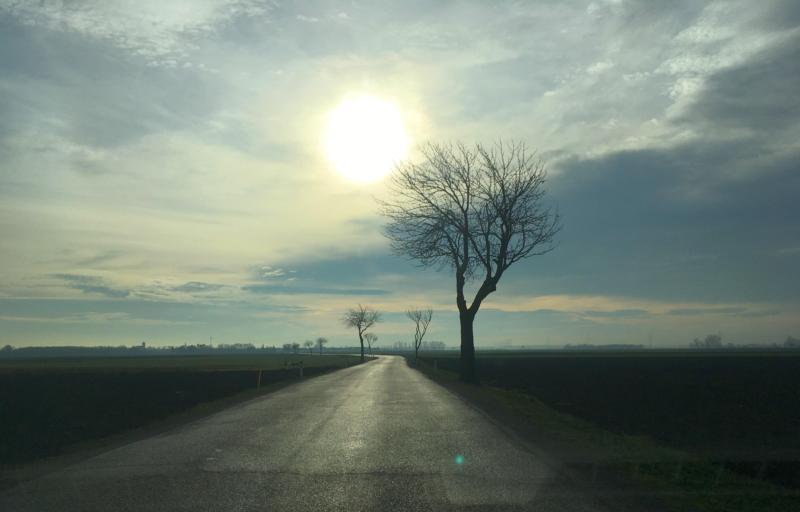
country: AT
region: Lower Austria
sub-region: Politischer Bezirk Ganserndorf
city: Andlersdorf
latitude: 48.2025
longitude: 16.6310
